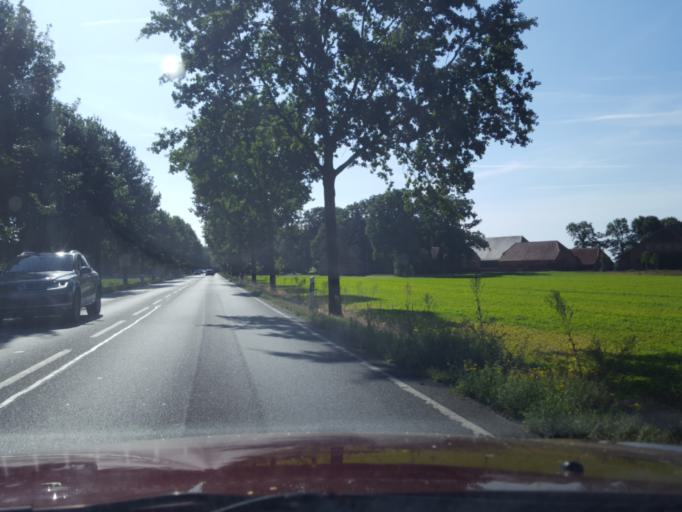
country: DE
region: Lower Saxony
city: Eystrup
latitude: 52.8001
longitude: 9.2091
